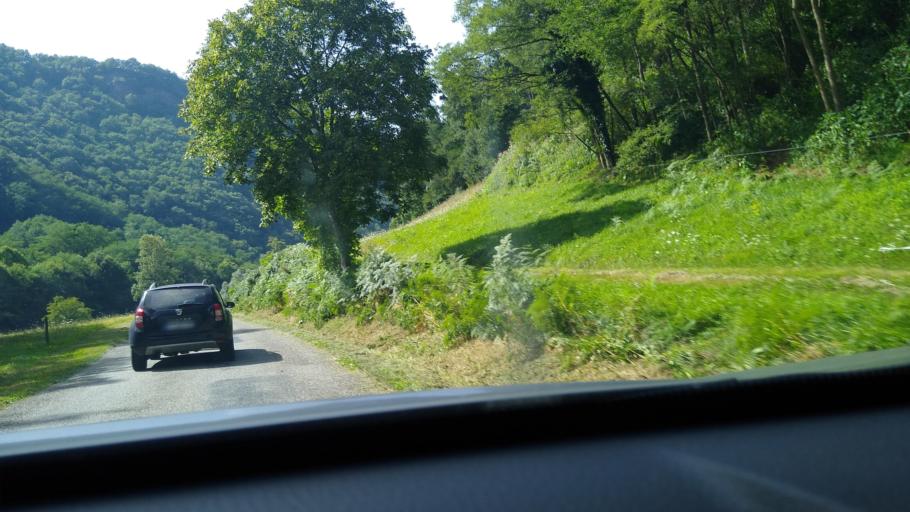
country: FR
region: Midi-Pyrenees
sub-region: Departement de l'Ariege
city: Saint-Girons
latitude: 42.9304
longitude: 1.1828
